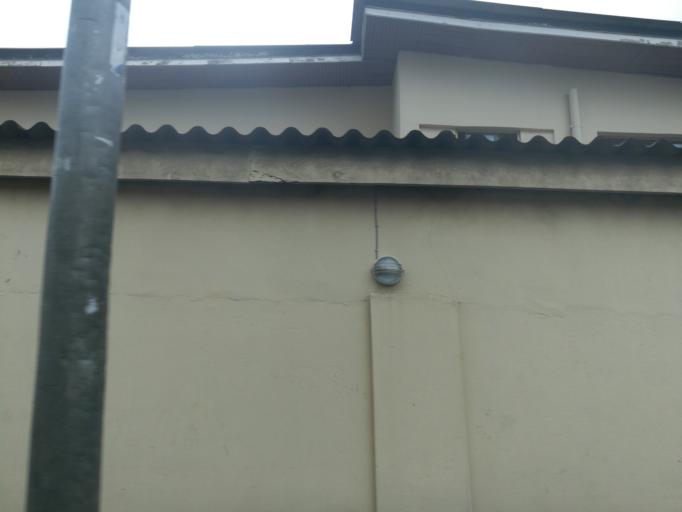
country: NG
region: Lagos
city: Ojota
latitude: 6.5703
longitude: 3.3718
